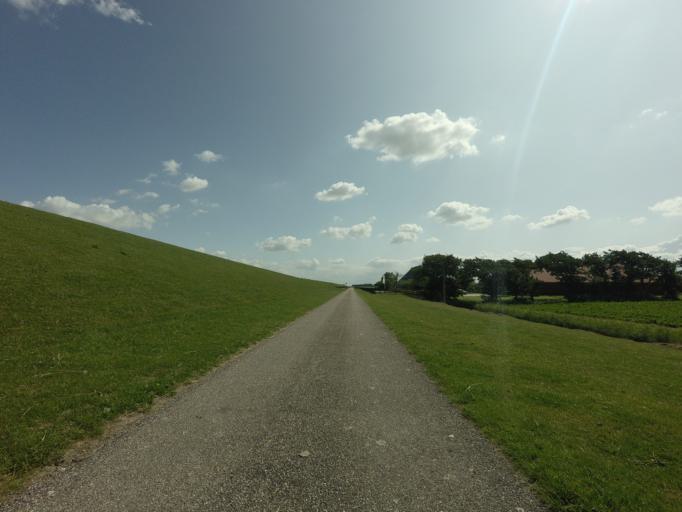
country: NL
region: Friesland
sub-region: Gemeente Ferwerderadiel
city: Hallum
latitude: 53.3234
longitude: 5.7388
